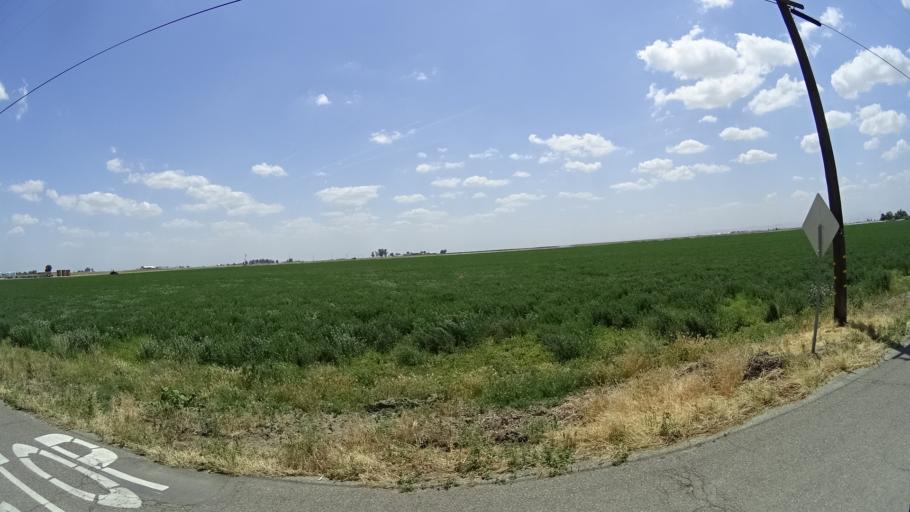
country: US
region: California
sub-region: Kings County
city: Stratford
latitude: 36.1818
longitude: -119.8272
